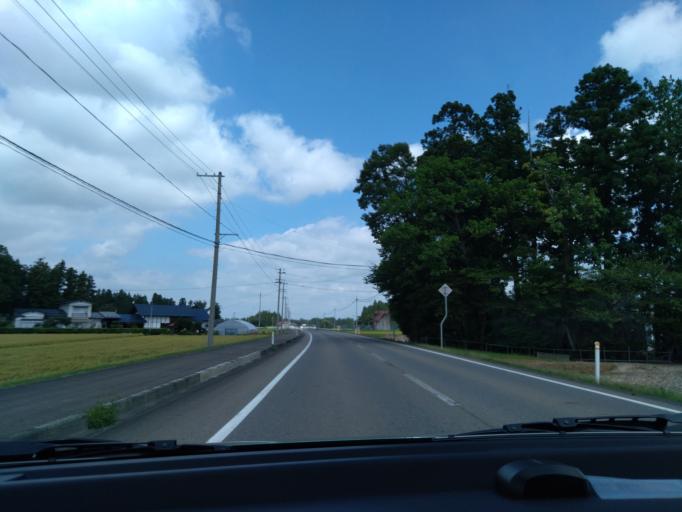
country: JP
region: Iwate
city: Hanamaki
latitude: 39.4118
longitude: 141.0743
